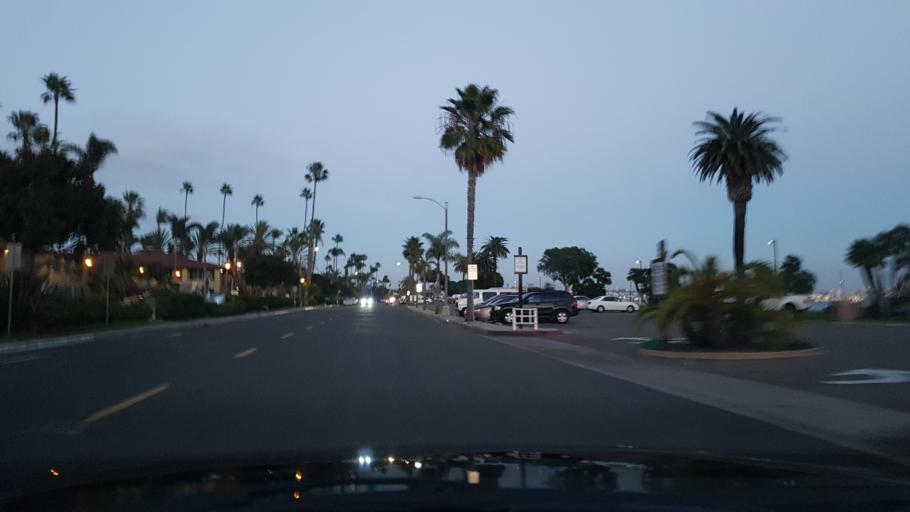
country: US
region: California
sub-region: San Diego County
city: Coronado
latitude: 32.7119
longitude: -117.2290
